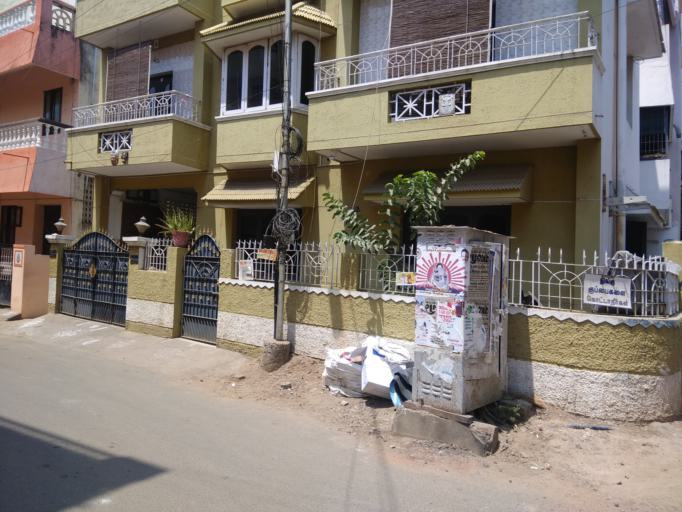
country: IN
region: Tamil Nadu
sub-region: Kancheepuram
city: Alandur
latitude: 13.0310
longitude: 80.2225
